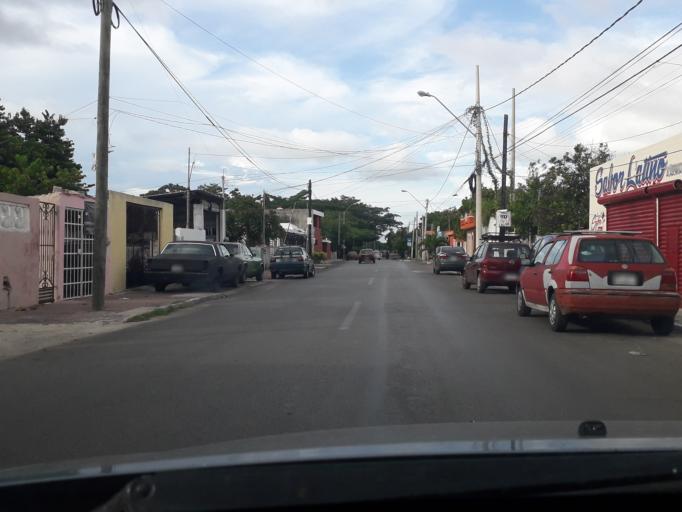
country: MX
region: Yucatan
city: Merida
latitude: 20.9744
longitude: -89.6630
